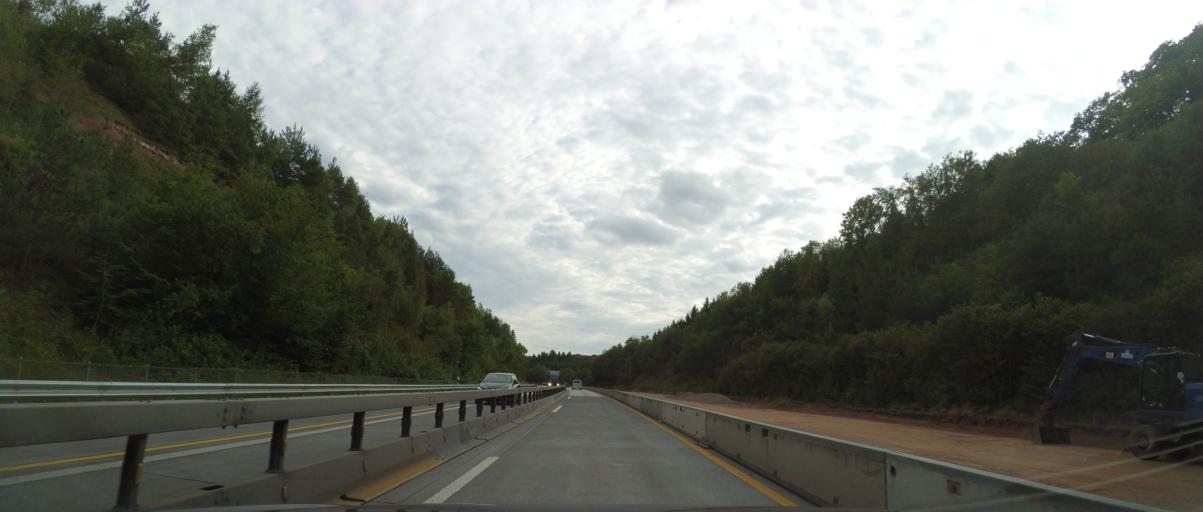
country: DE
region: Rheinland-Pfalz
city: Wittlich
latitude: 49.9596
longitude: 6.8845
